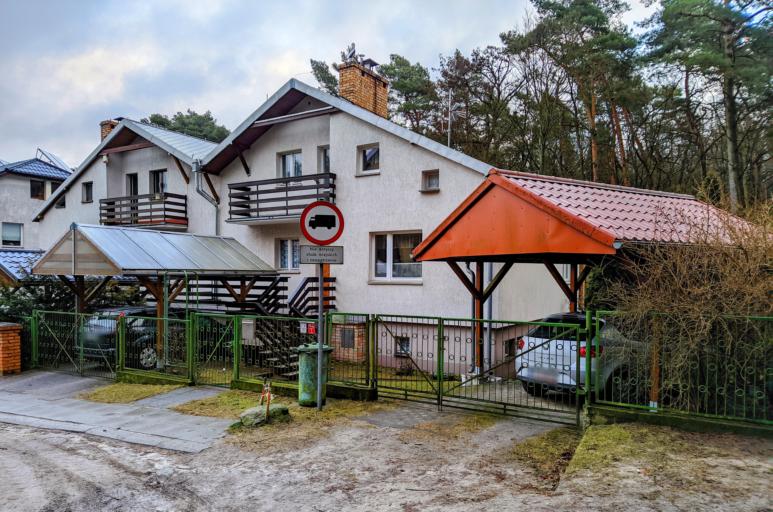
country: PL
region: Lubusz
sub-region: Zielona Gora
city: Zielona Gora
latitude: 51.9346
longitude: 15.5404
